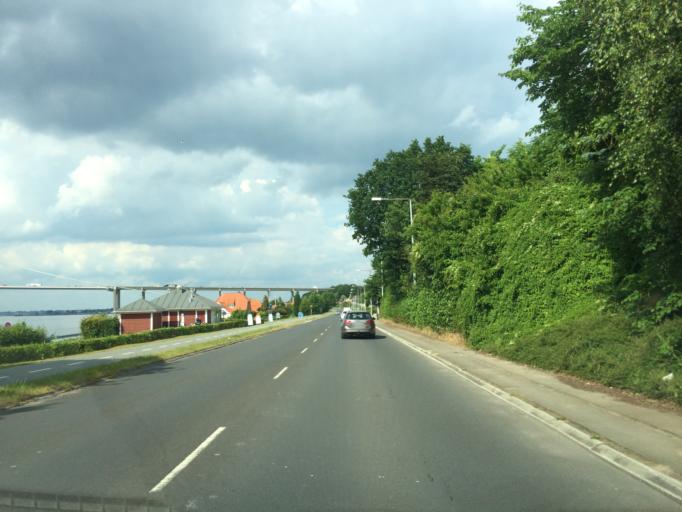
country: DK
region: South Denmark
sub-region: Middelfart Kommune
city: Middelfart
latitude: 55.5099
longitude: 9.7552
